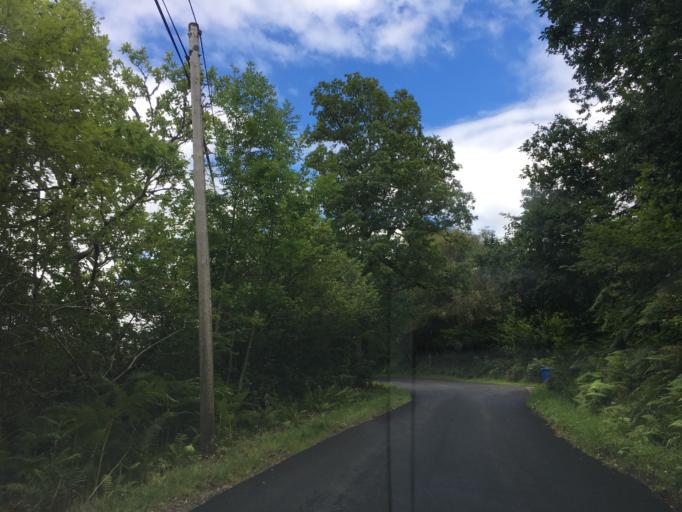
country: GB
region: Scotland
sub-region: Argyll and Bute
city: Oban
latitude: 56.3427
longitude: -5.1962
